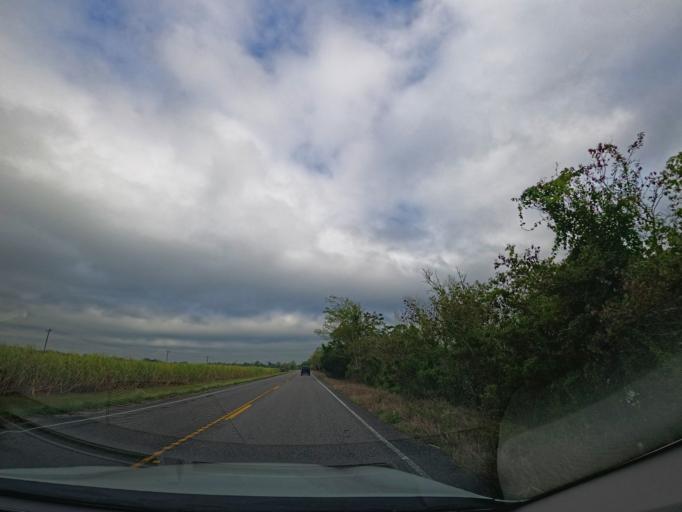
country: US
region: Louisiana
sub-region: Terrebonne Parish
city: Bayou Cane
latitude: 29.5968
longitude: -90.8285
